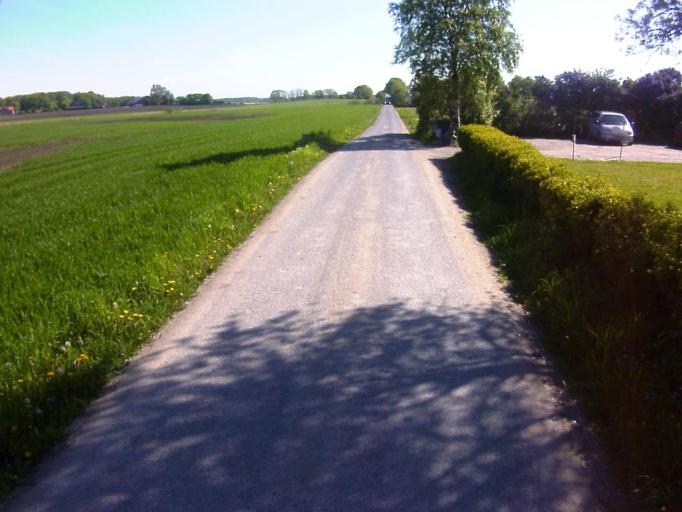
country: SE
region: Blekinge
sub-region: Solvesborgs Kommun
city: Soelvesborg
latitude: 56.0685
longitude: 14.6130
